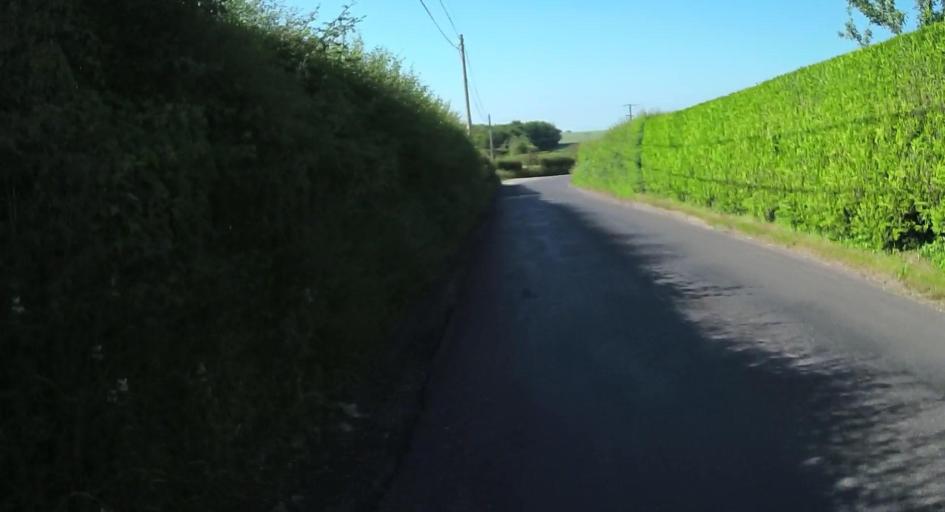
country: GB
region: England
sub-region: Hampshire
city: Kings Worthy
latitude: 51.0629
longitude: -1.2762
